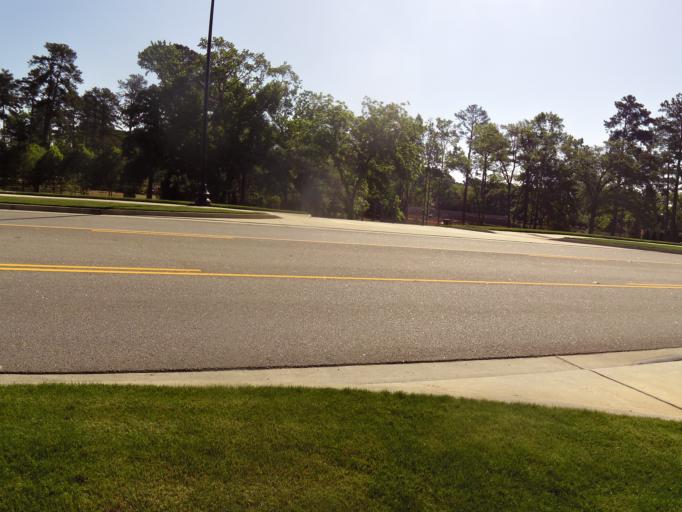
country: US
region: Georgia
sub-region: Columbia County
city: Martinez
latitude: 33.5024
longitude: -82.0309
